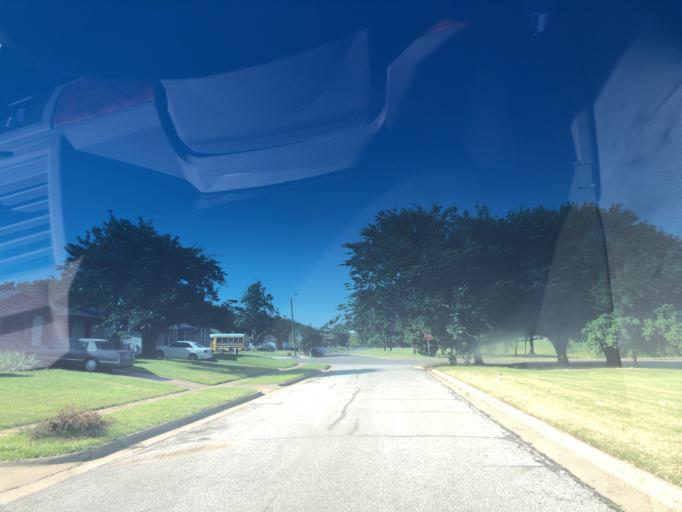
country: US
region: Texas
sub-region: Dallas County
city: Grand Prairie
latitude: 32.7299
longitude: -97.0385
